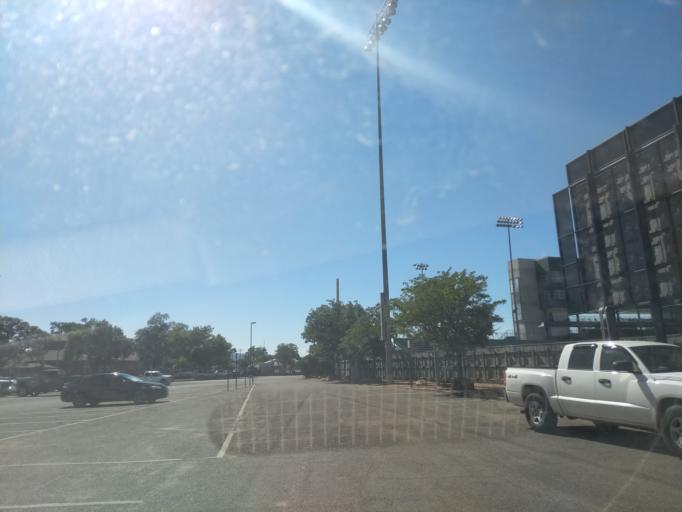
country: US
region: Colorado
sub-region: Mesa County
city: Grand Junction
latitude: 39.0756
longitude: -108.5498
